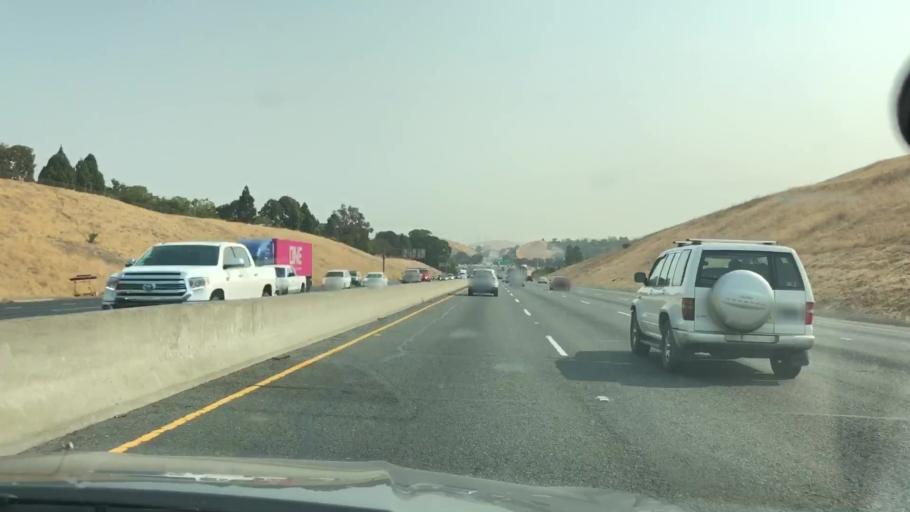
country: US
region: California
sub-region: Contra Costa County
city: Hercules
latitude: 38.0044
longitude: -122.2798
